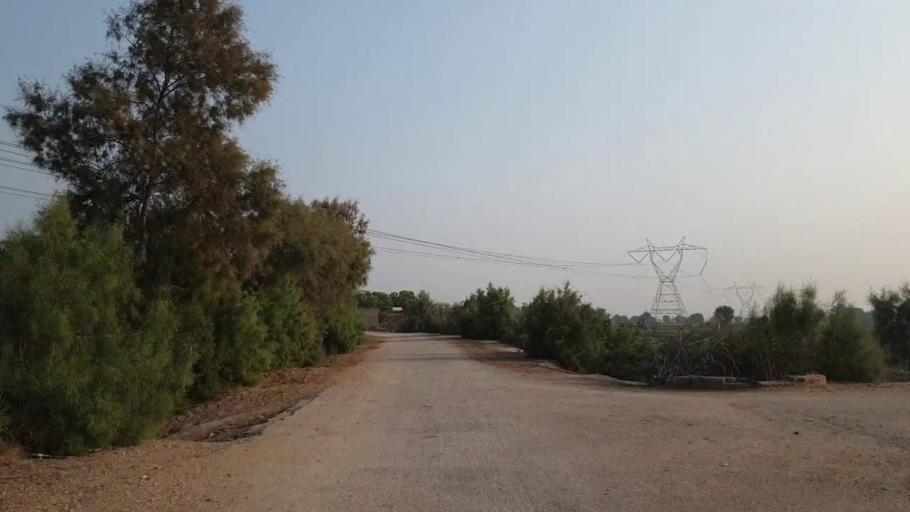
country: PK
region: Sindh
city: Bhan
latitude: 26.4926
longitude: 67.7721
